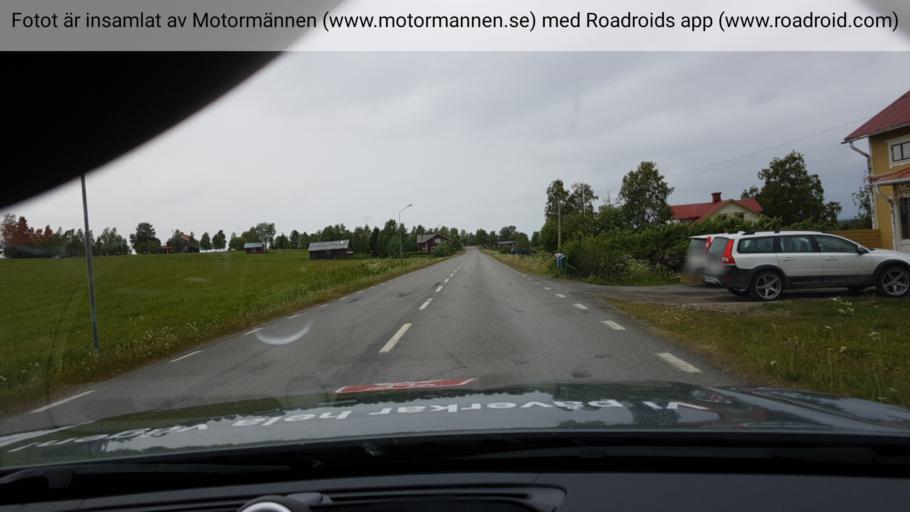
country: SE
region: Jaemtland
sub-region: Stroemsunds Kommun
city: Stroemsund
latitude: 63.6242
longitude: 15.2487
